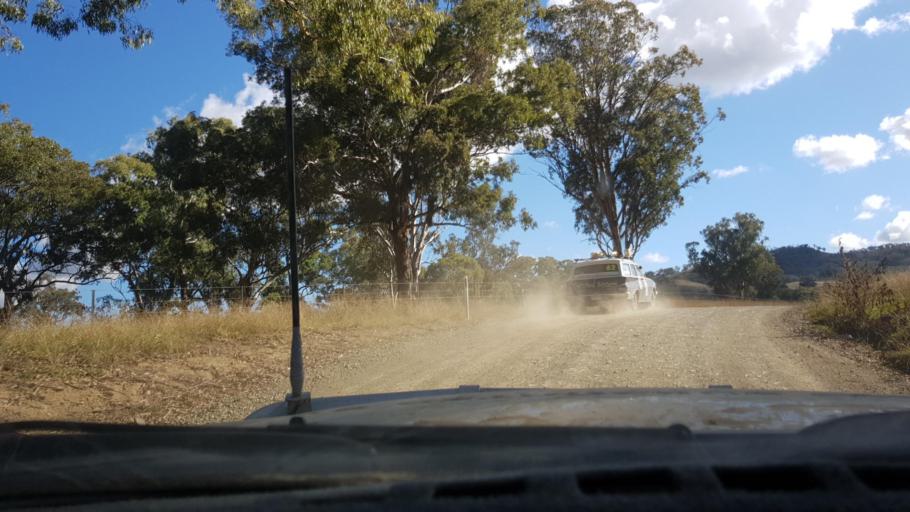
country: AU
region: New South Wales
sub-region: Tamworth Municipality
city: Manilla
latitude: -30.6189
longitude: 150.5150
